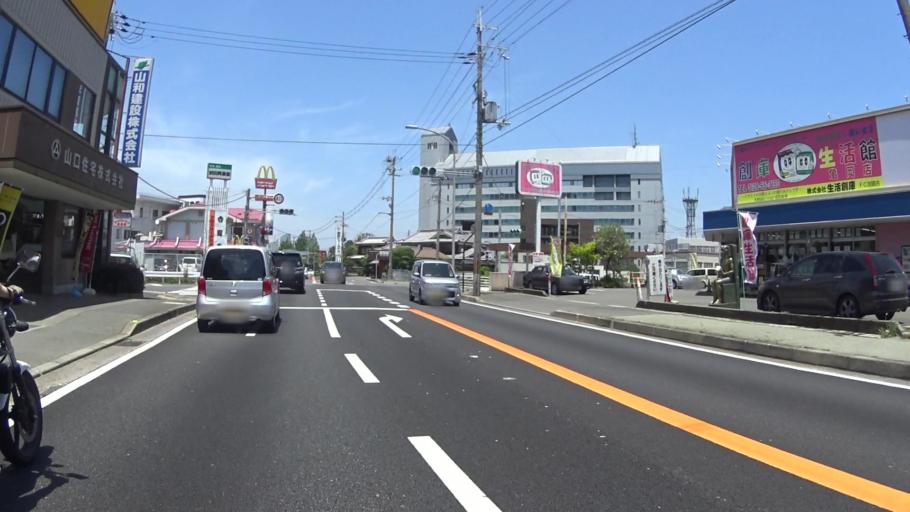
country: JP
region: Kyoto
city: Kameoka
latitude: 35.0119
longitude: 135.5741
